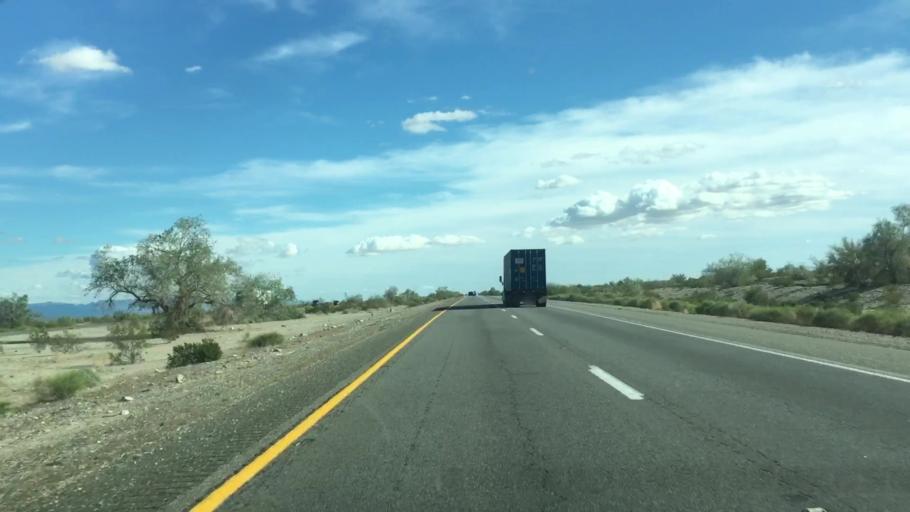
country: US
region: California
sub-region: Imperial County
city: Niland
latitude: 33.6980
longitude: -115.2969
